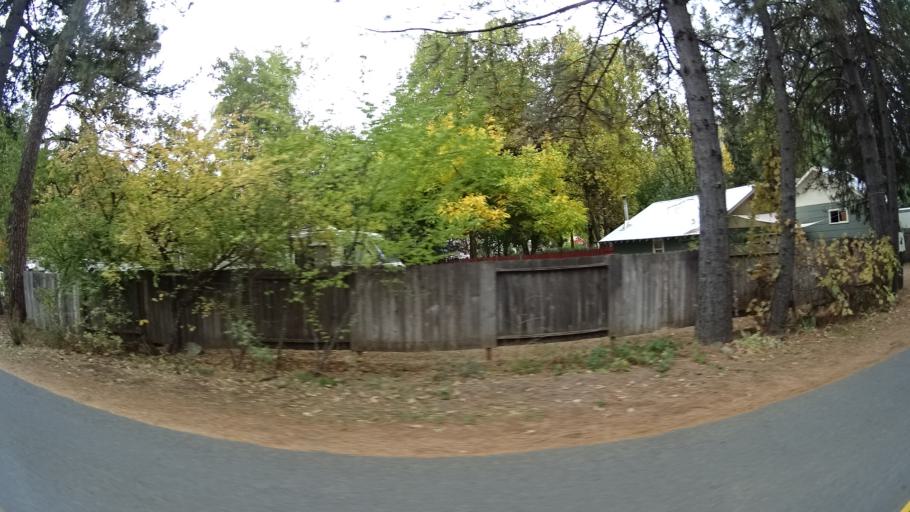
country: US
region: California
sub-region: Siskiyou County
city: Happy Camp
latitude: 41.7995
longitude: -123.3773
